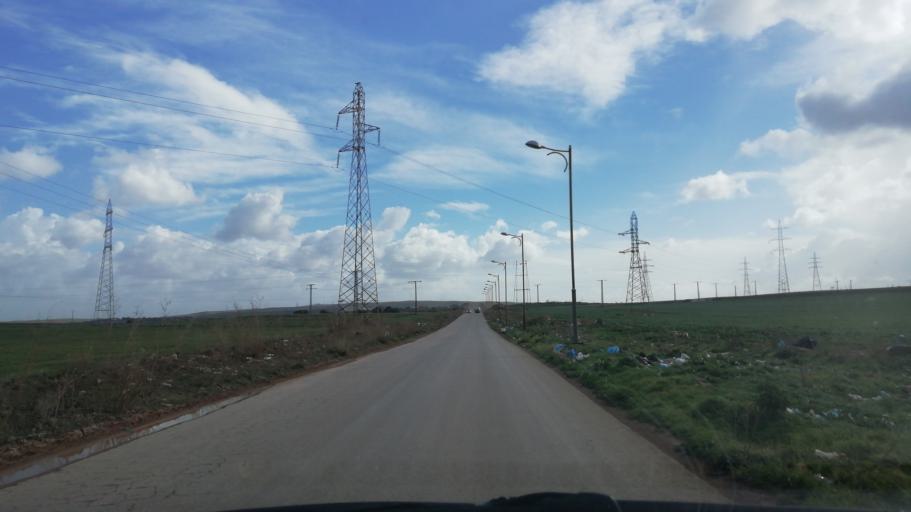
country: DZ
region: Oran
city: Sidi ech Chahmi
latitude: 35.6365
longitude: -0.5446
